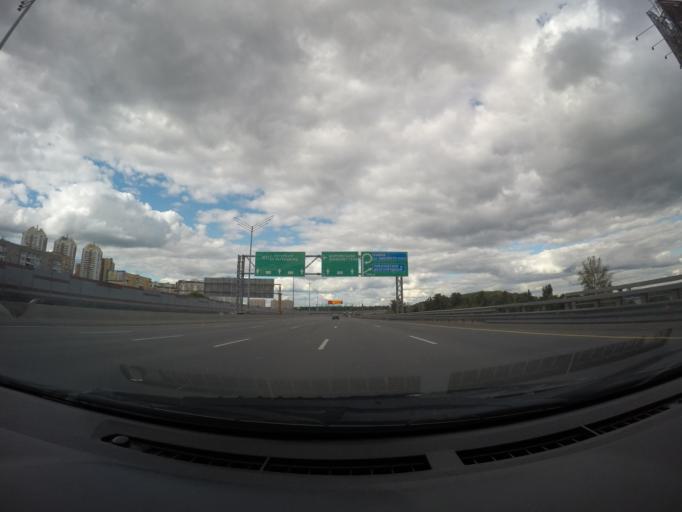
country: RU
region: Moskovskaya
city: Levoberezhnaya
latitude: 55.8928
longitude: 37.4857
